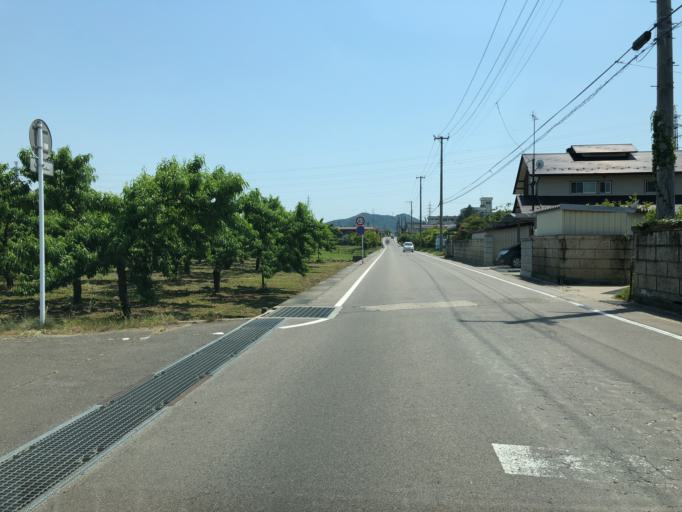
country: JP
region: Fukushima
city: Fukushima-shi
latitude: 37.8097
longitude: 140.4741
